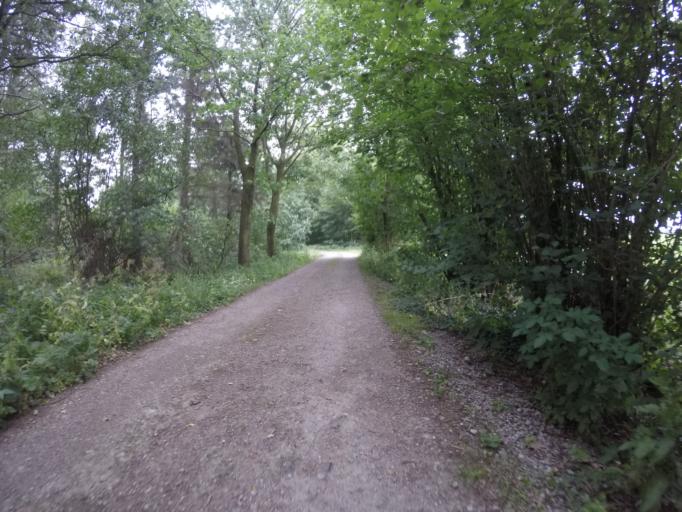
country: NL
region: Gelderland
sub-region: Oude IJsselstreek
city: Gendringen
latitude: 51.8658
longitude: 6.4132
